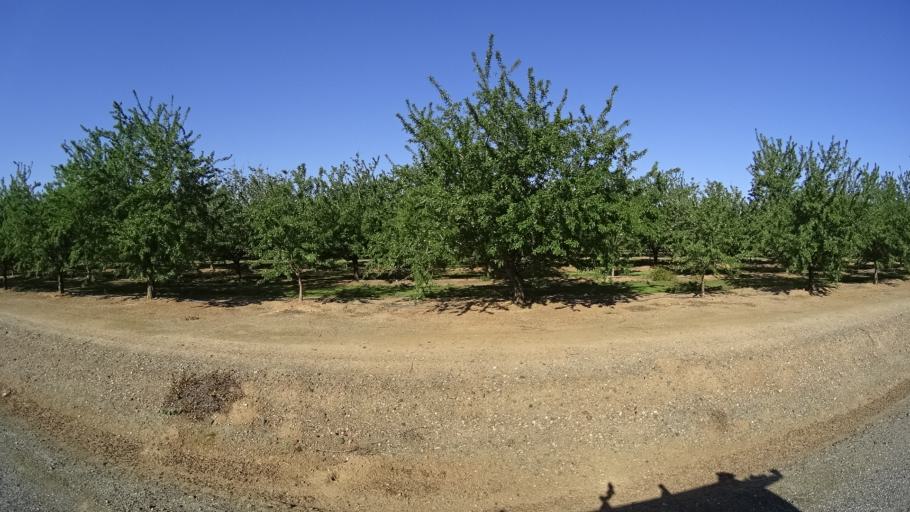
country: US
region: California
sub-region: Glenn County
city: Hamilton City
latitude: 39.7843
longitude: -122.0854
